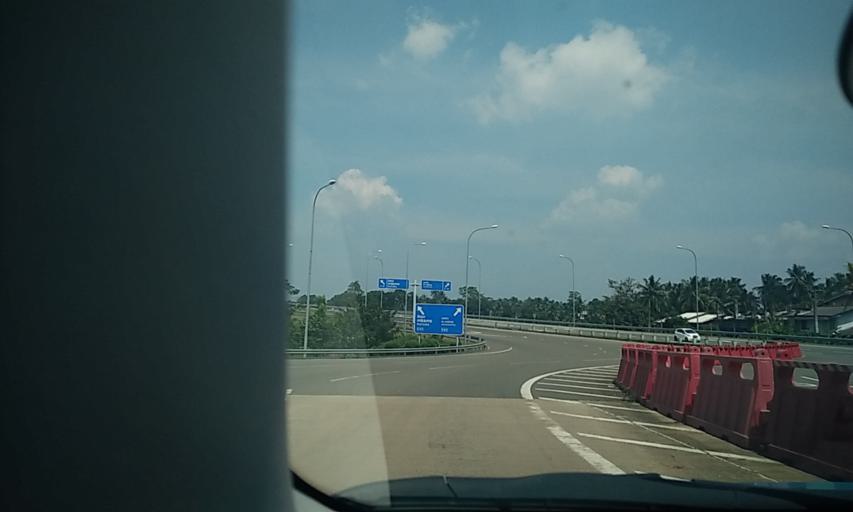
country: LK
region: Western
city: Homagama
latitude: 6.8401
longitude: 79.9815
